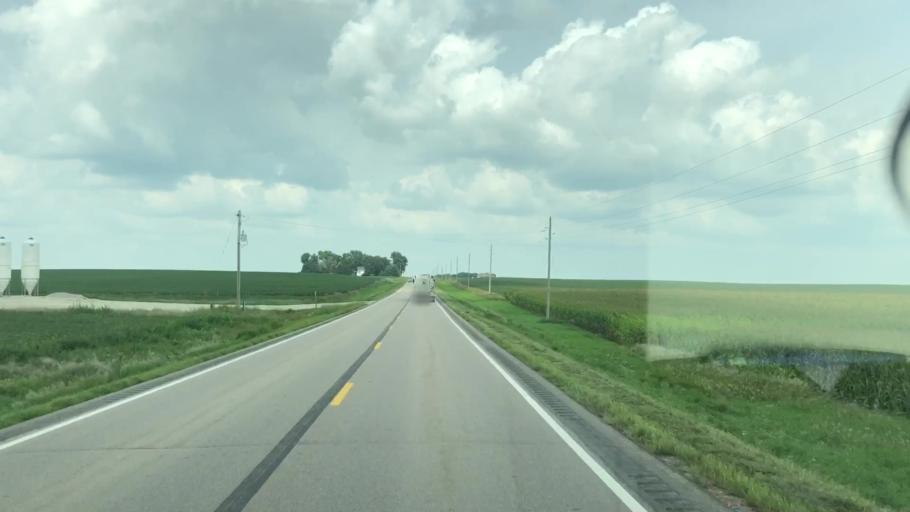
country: US
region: Iowa
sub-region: Plymouth County
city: Remsen
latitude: 42.7849
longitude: -95.9578
